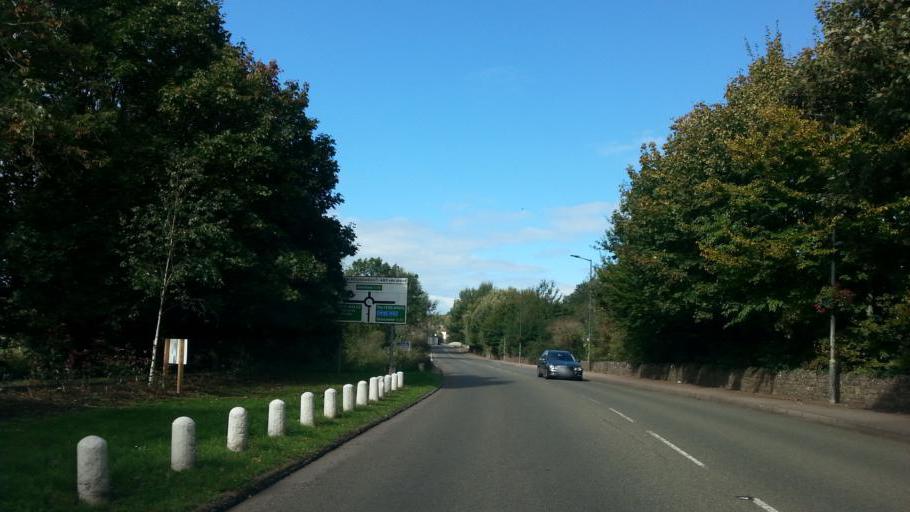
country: GB
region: England
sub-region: Herefordshire
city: Ross on Wye
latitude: 51.9138
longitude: -2.5946
